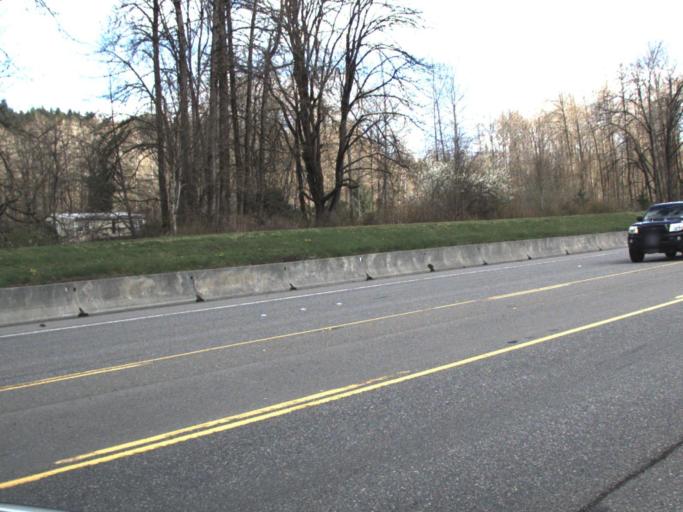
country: US
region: Washington
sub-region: King County
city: East Renton Highlands
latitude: 47.4643
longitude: -122.1316
